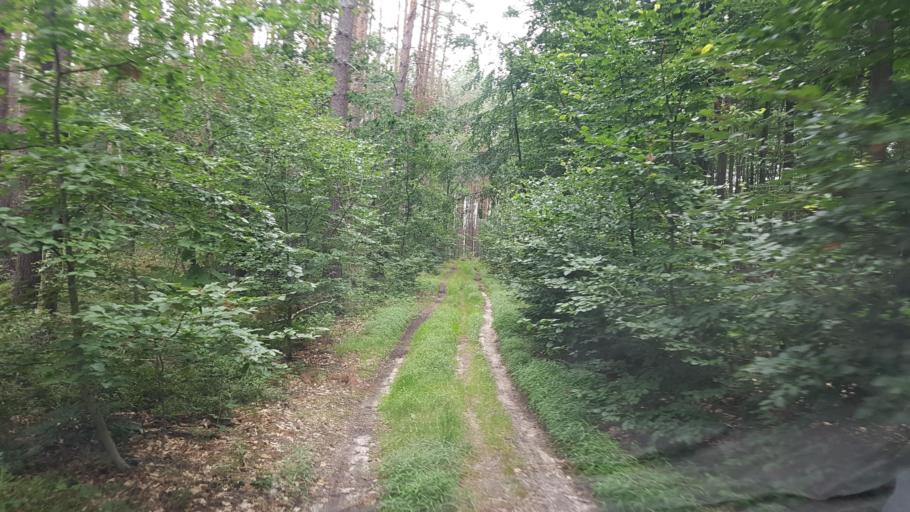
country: DE
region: Brandenburg
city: Crinitz
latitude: 51.7322
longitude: 13.7421
